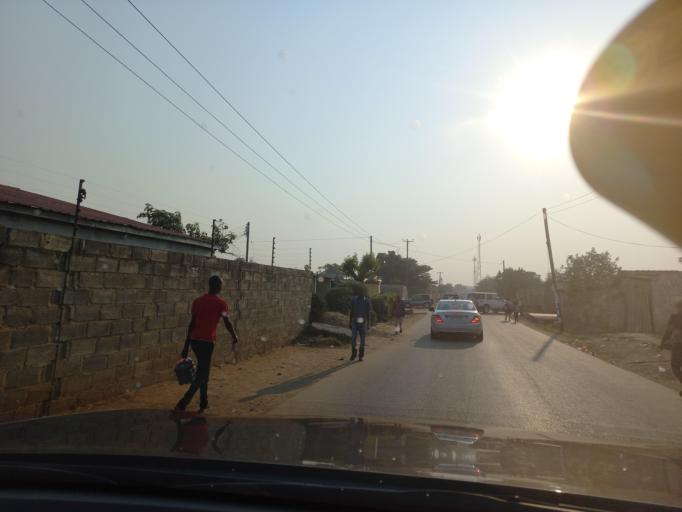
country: ZM
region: Lusaka
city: Lusaka
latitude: -15.4051
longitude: 28.3447
